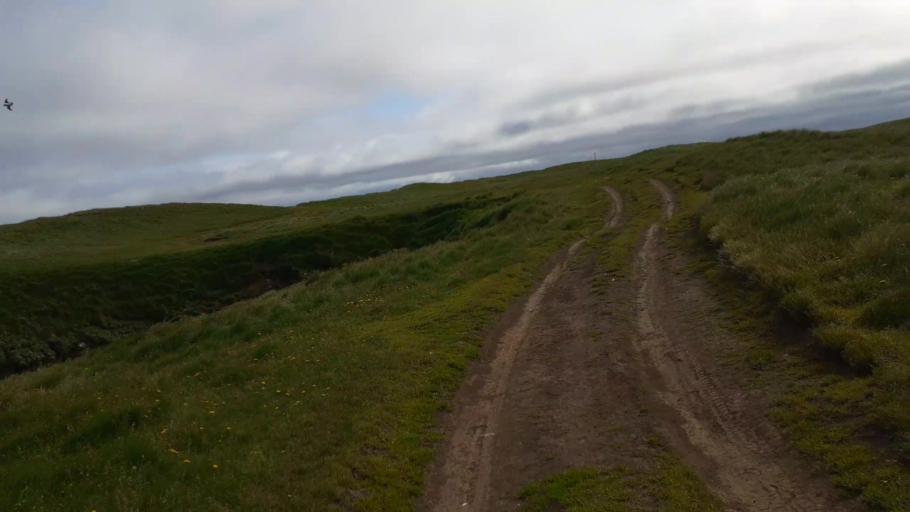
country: IS
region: Northeast
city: Dalvik
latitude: 66.5567
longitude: -18.0046
